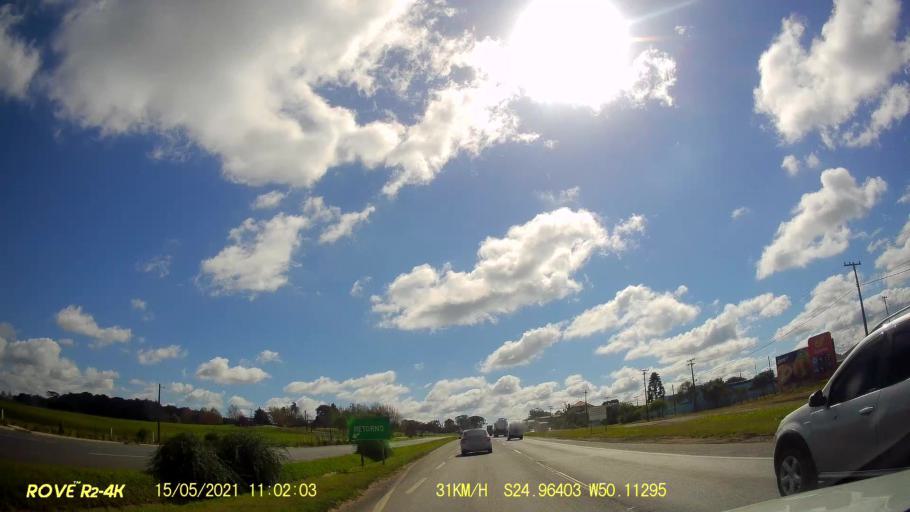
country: BR
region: Parana
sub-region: Carambei
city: Carambei
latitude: -24.9643
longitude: -50.1129
